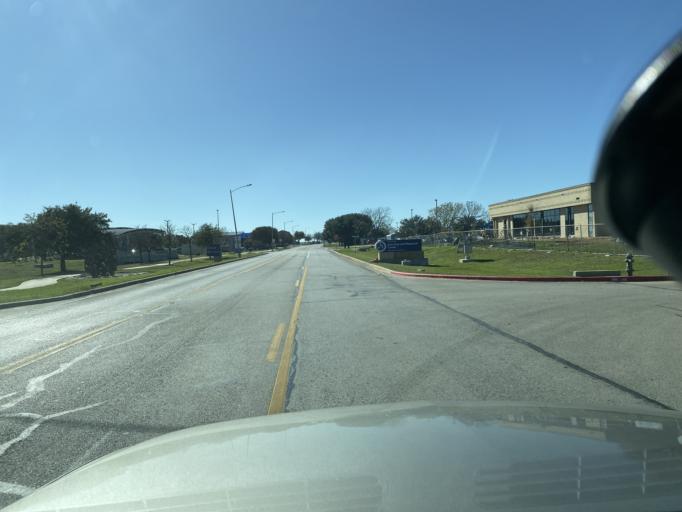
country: US
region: Texas
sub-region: Travis County
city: Hornsby Bend
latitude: 30.2125
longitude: -97.6664
